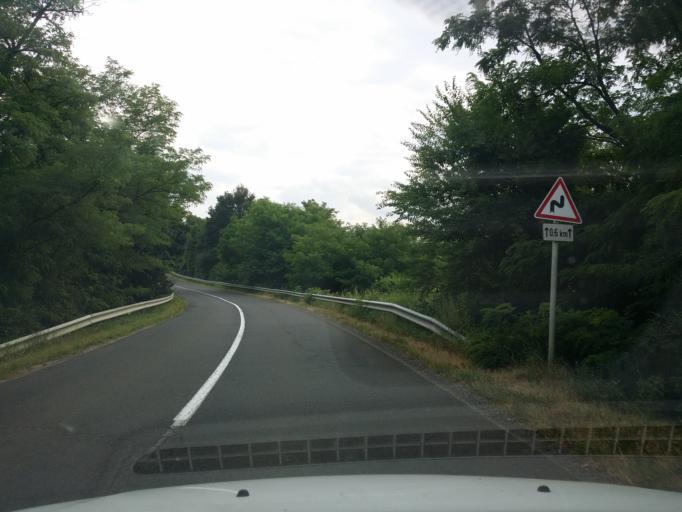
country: HU
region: Nograd
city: Bercel
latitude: 47.9330
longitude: 19.3660
